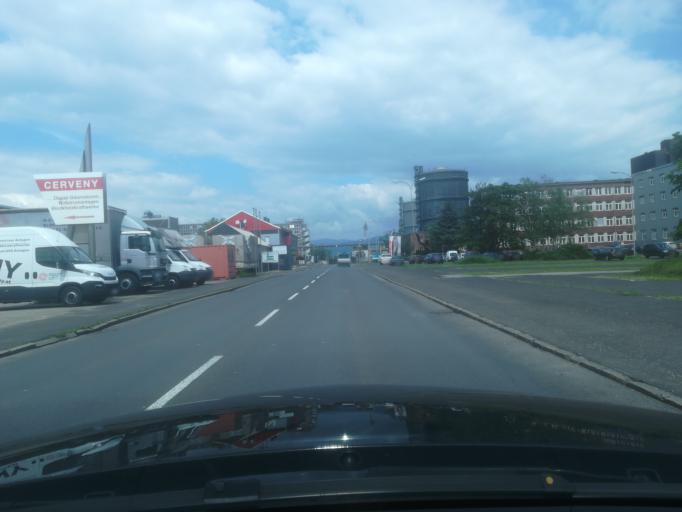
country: AT
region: Upper Austria
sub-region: Politischer Bezirk Urfahr-Umgebung
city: Steyregg
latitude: 48.2722
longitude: 14.3239
